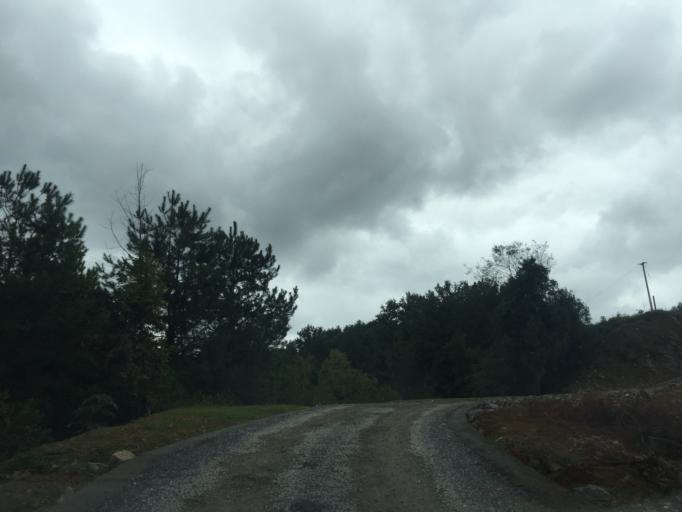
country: CN
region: Guizhou Sheng
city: Xujiaba
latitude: 27.6932
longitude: 108.1096
